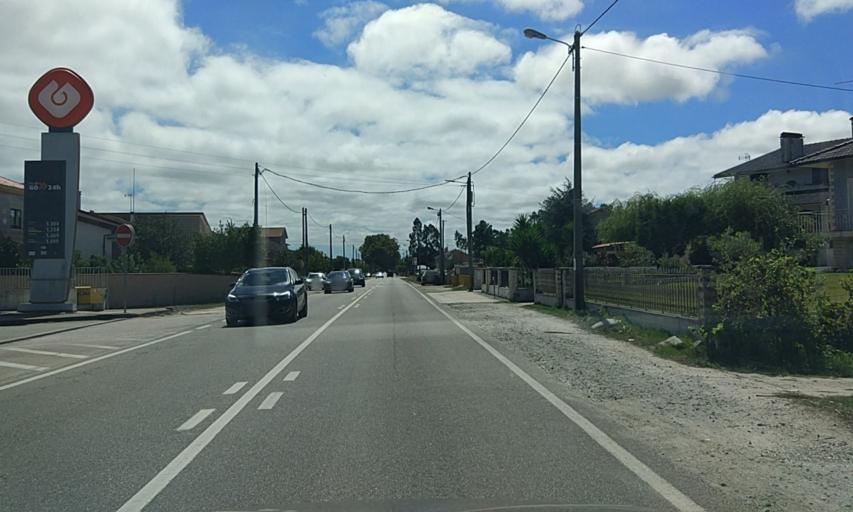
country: PT
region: Aveiro
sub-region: Vagos
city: Vagos
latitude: 40.5196
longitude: -8.6790
